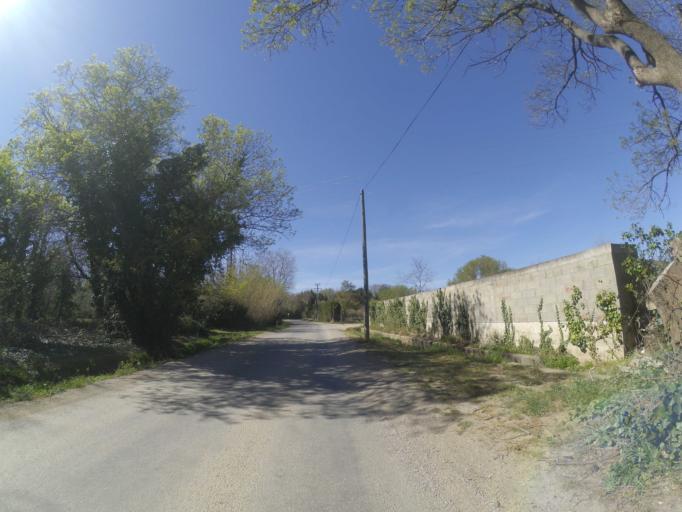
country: FR
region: Languedoc-Roussillon
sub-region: Departement des Pyrenees-Orientales
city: Toulouges
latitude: 42.6730
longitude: 2.8212
